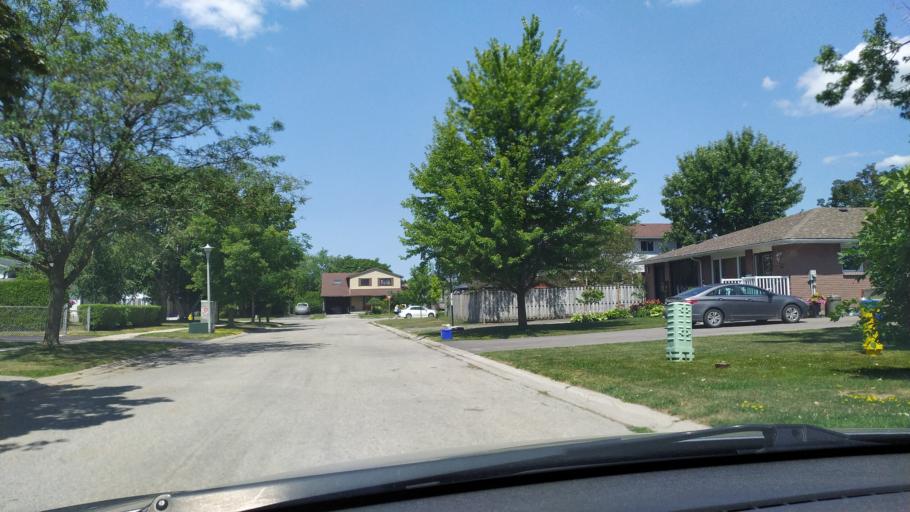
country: CA
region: Ontario
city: Stratford
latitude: 43.3558
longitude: -80.9795
